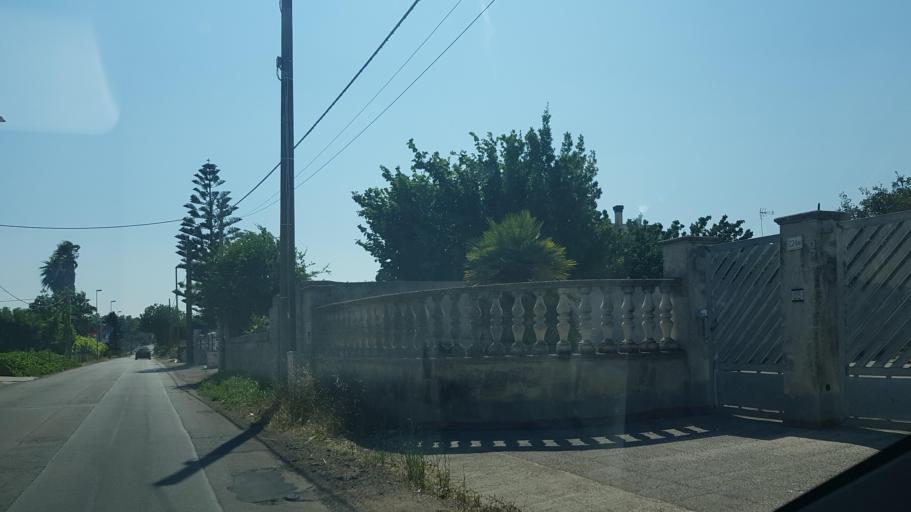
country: IT
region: Apulia
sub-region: Provincia di Lecce
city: Taurisano
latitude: 39.9530
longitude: 18.2045
